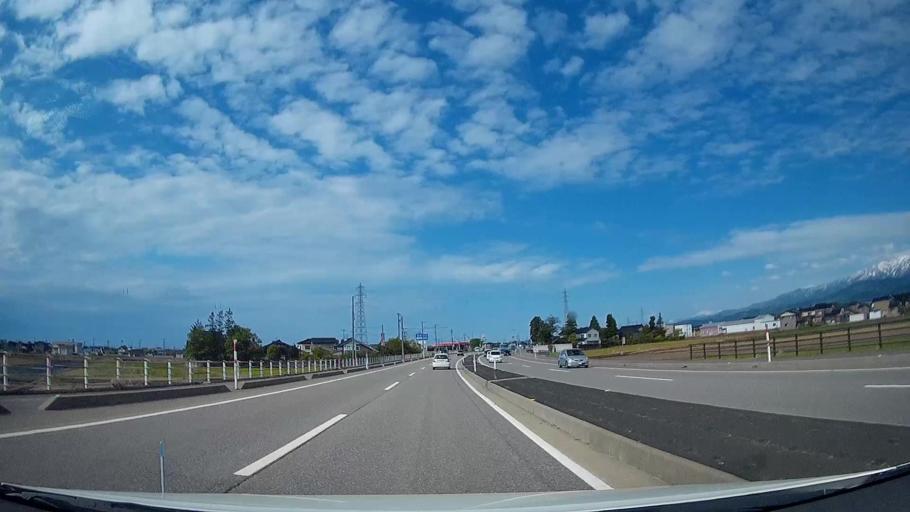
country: JP
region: Toyama
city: Namerikawa
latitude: 36.7441
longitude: 137.3452
